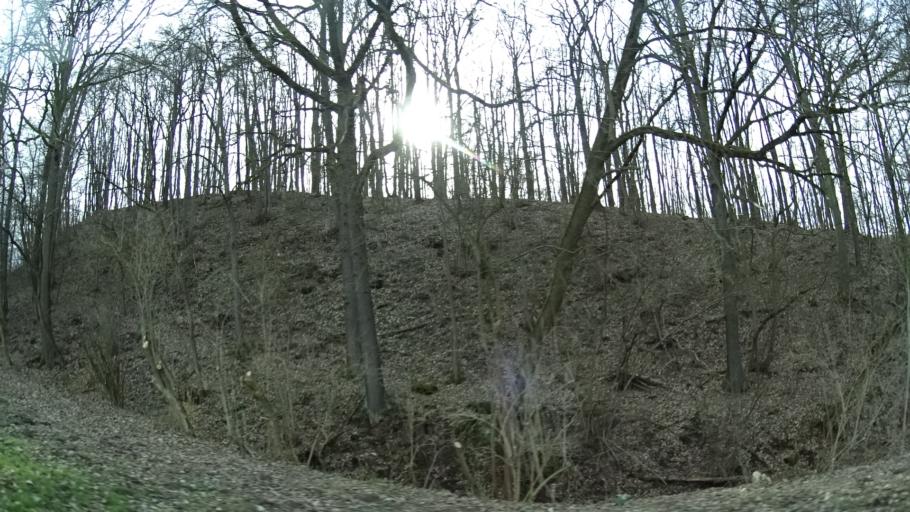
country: DE
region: Thuringia
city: Sulza
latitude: 50.8689
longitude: 11.6230
